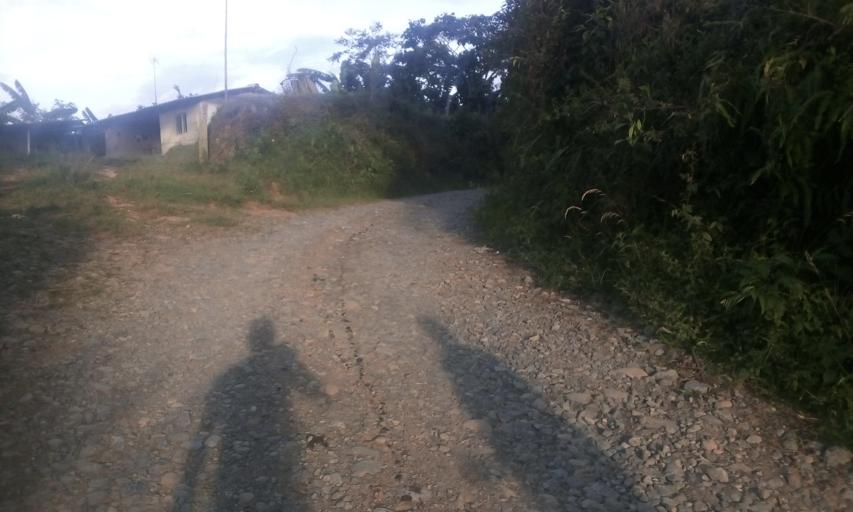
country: CO
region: Boyaca
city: Santana
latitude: 6.0037
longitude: -73.5043
